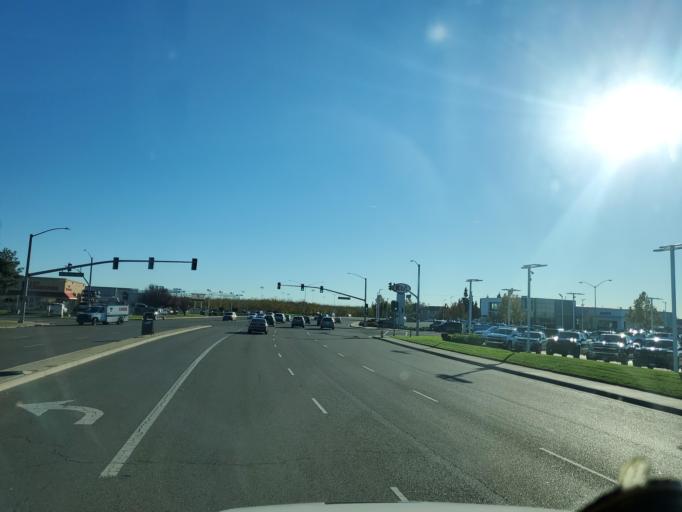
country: US
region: California
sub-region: San Joaquin County
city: Morada
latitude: 38.0182
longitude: -121.2706
